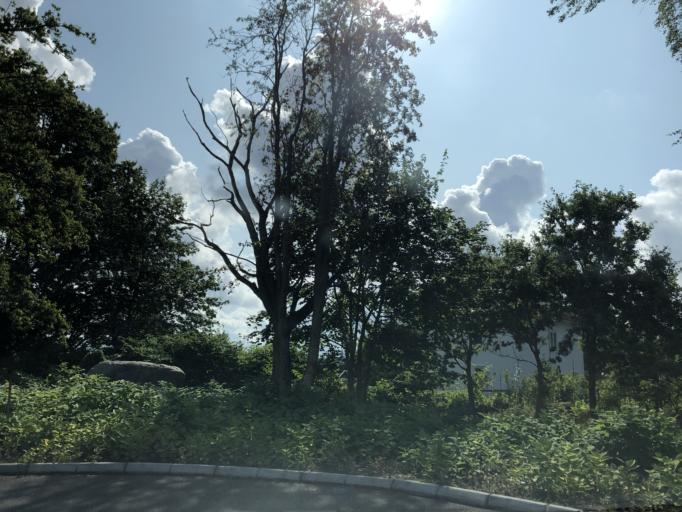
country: SE
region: Vaestra Goetaland
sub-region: Goteborg
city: Majorna
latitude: 57.7098
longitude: 11.8999
